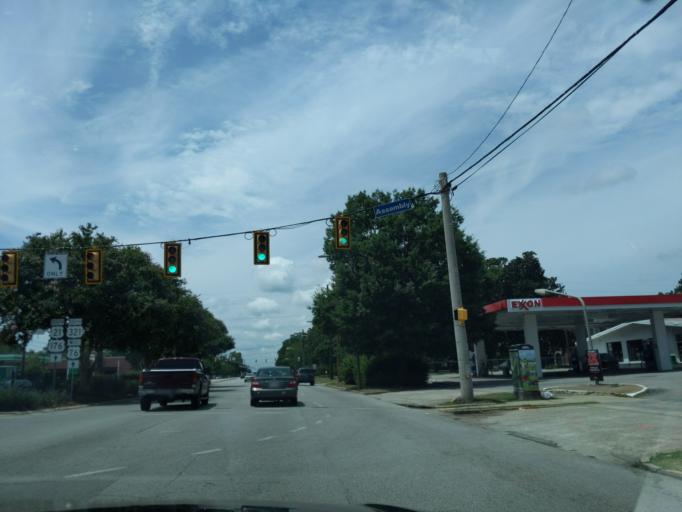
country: US
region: South Carolina
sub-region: Richland County
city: Columbia
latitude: 34.0130
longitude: -81.0406
